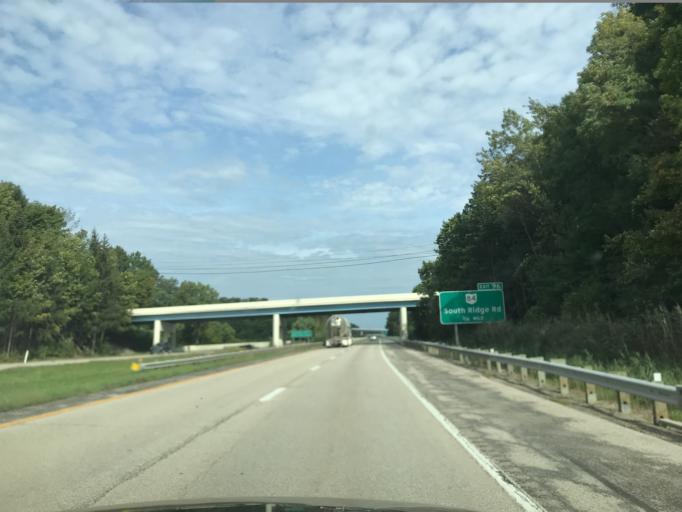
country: US
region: Ohio
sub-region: Ashtabula County
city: Edgewood
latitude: 41.8508
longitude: -80.7674
